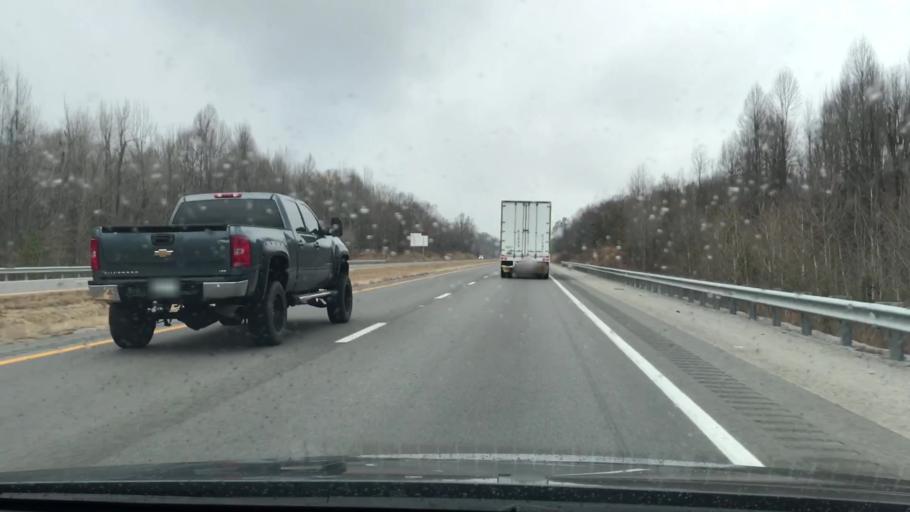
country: US
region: Kentucky
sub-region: Hopkins County
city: Earlington
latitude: 37.2694
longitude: -87.4540
